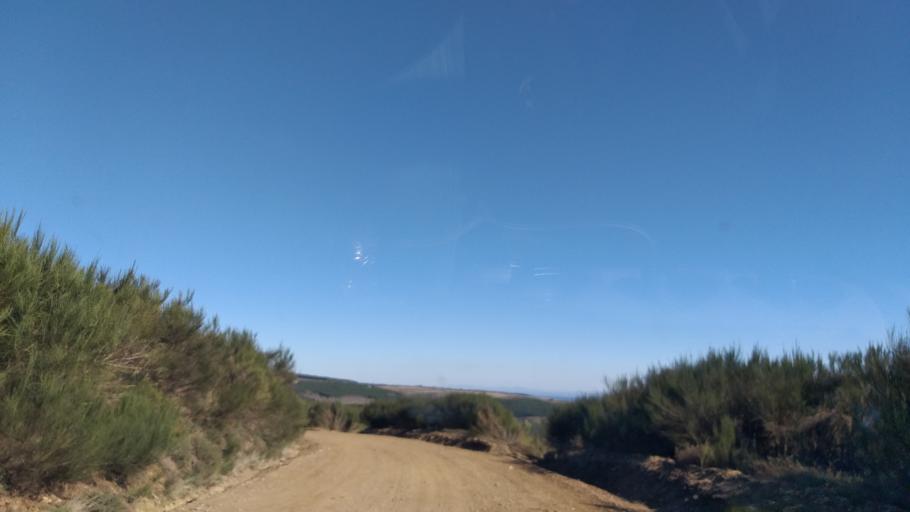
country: PT
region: Guarda
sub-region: Manteigas
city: Manteigas
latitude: 40.5048
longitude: -7.4755
